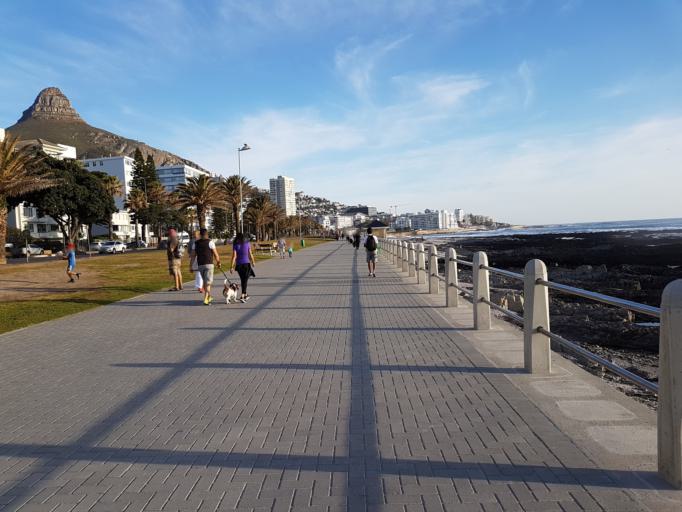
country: ZA
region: Western Cape
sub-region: City of Cape Town
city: Cape Town
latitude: -33.9129
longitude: 18.3879
